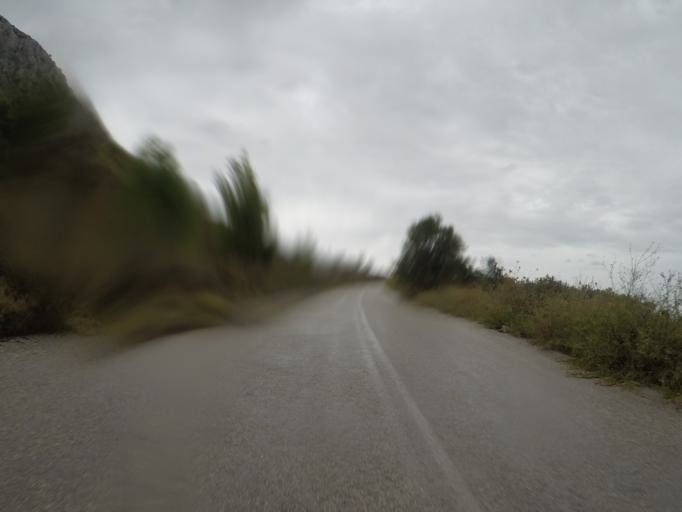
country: GR
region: Peloponnese
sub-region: Nomos Korinthias
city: Arkhaia Korinthos
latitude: 37.8985
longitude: 22.8808
